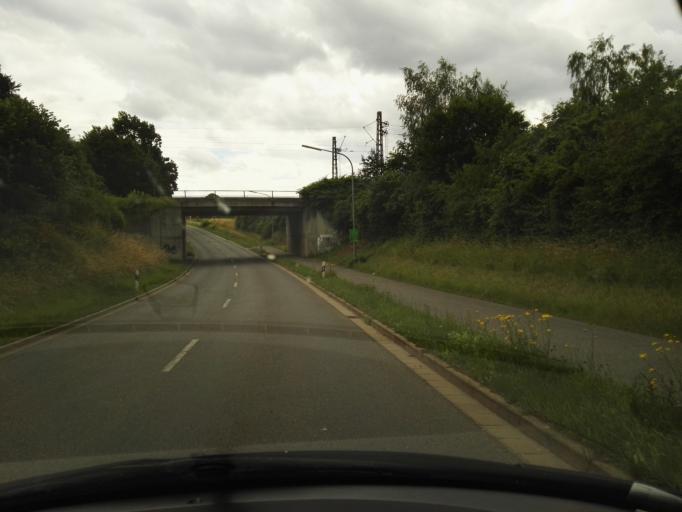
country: DE
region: Bavaria
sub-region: Upper Franconia
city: Redwitz an der Rodach
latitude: 50.1683
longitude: 11.2029
